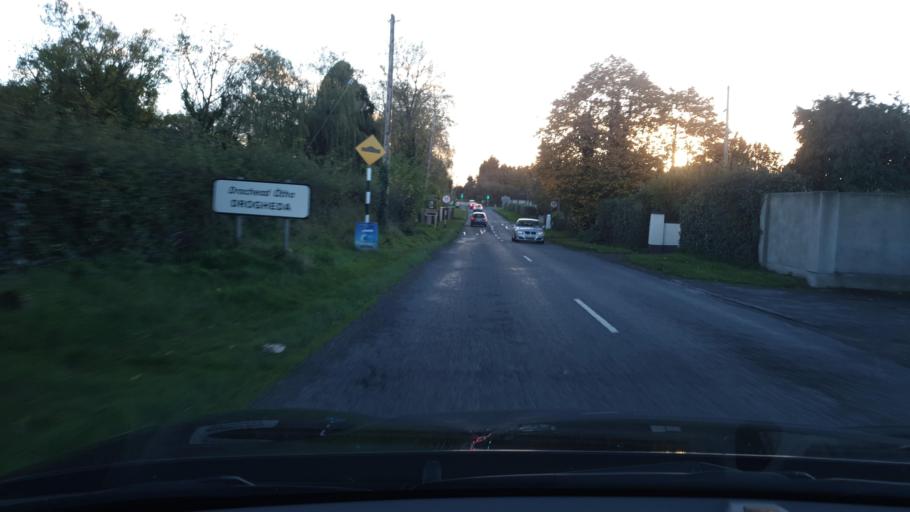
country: IE
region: Leinster
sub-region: Lu
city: Drogheda
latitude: 53.7291
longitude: -6.3231
